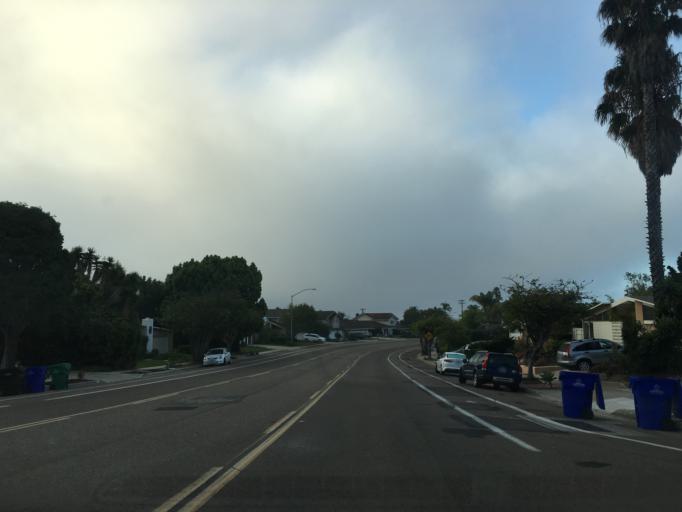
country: US
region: California
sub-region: San Diego County
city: La Jolla
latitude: 32.8222
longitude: -117.2347
